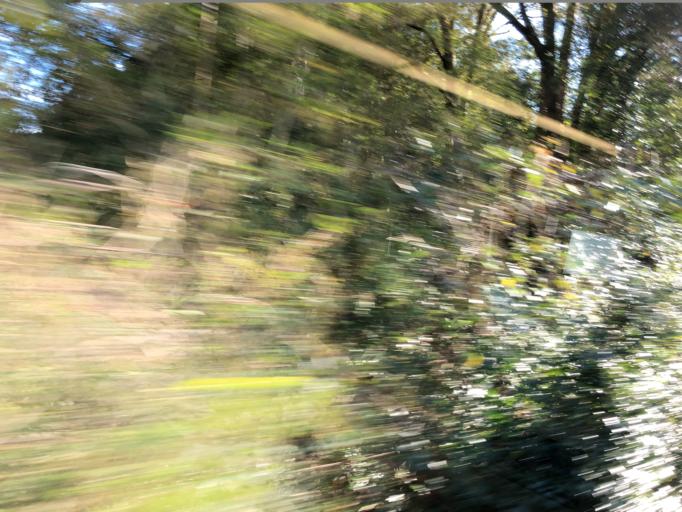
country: JP
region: Kochi
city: Nakamura
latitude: 33.1170
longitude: 133.1134
